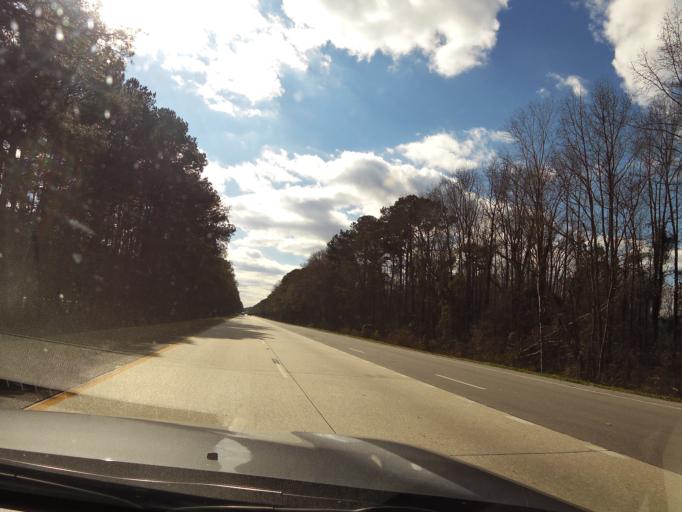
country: US
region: South Carolina
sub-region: Florence County
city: Timmonsville
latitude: 34.1090
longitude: -79.9141
